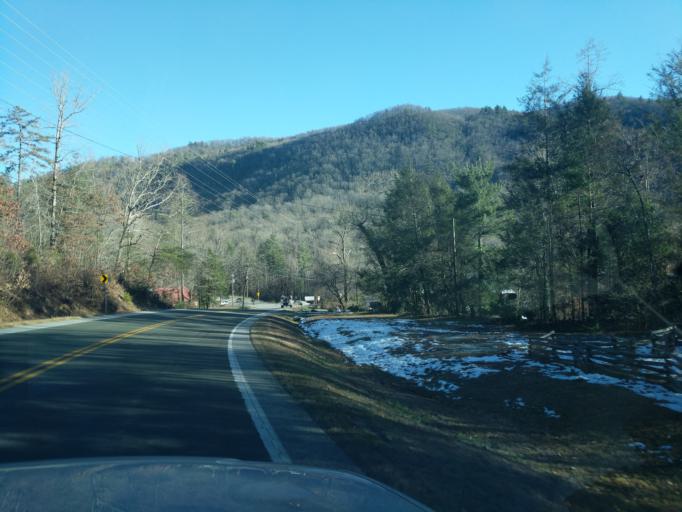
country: US
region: Georgia
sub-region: Rabun County
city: Clayton
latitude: 34.8604
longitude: -83.5135
